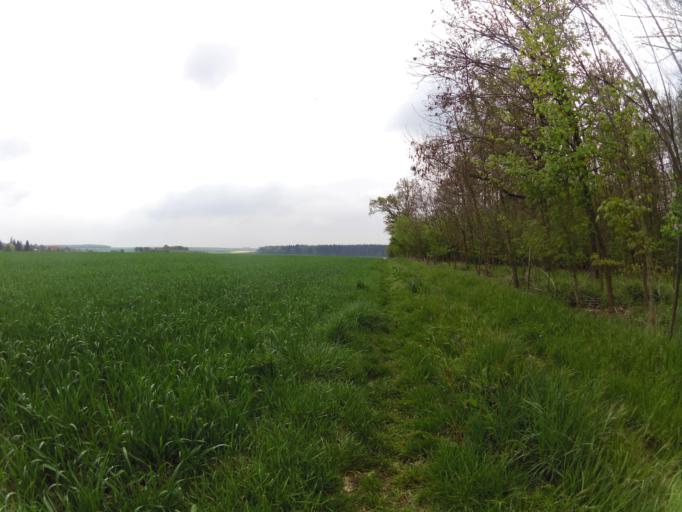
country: DE
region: Bavaria
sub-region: Regierungsbezirk Unterfranken
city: Frickenhausen
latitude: 49.7064
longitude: 10.0722
